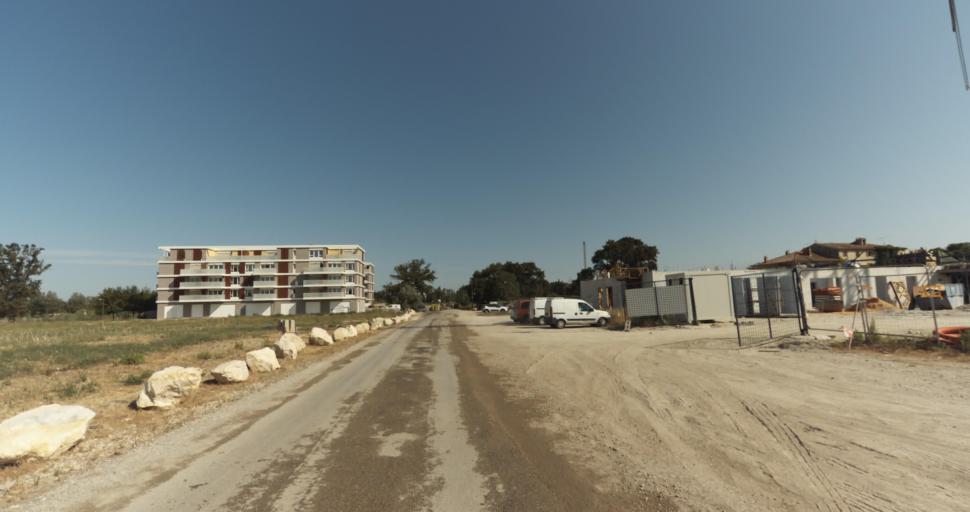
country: FR
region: Provence-Alpes-Cote d'Azur
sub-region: Departement du Vaucluse
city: Althen-des-Paluds
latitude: 44.0163
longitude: 4.9695
